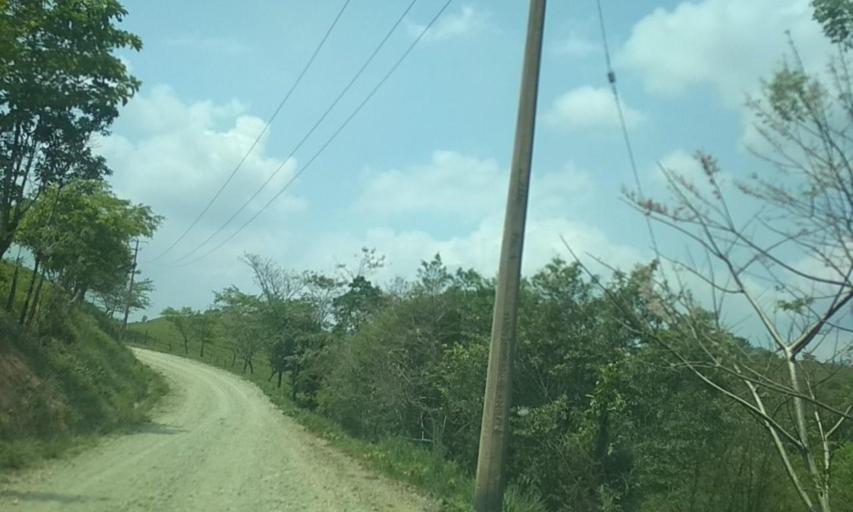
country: MX
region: Tabasco
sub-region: Huimanguillo
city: Francisco Rueda
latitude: 17.6235
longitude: -93.8169
